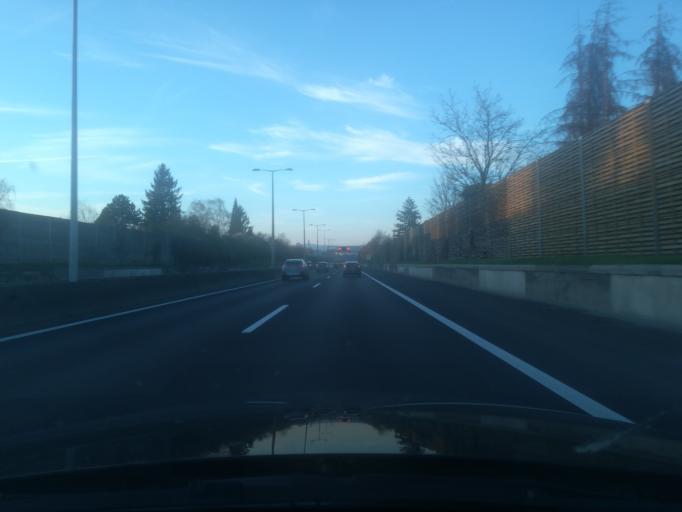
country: AT
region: Upper Austria
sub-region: Politischer Bezirk Linz-Land
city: Ansfelden
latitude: 48.2526
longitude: 14.2973
